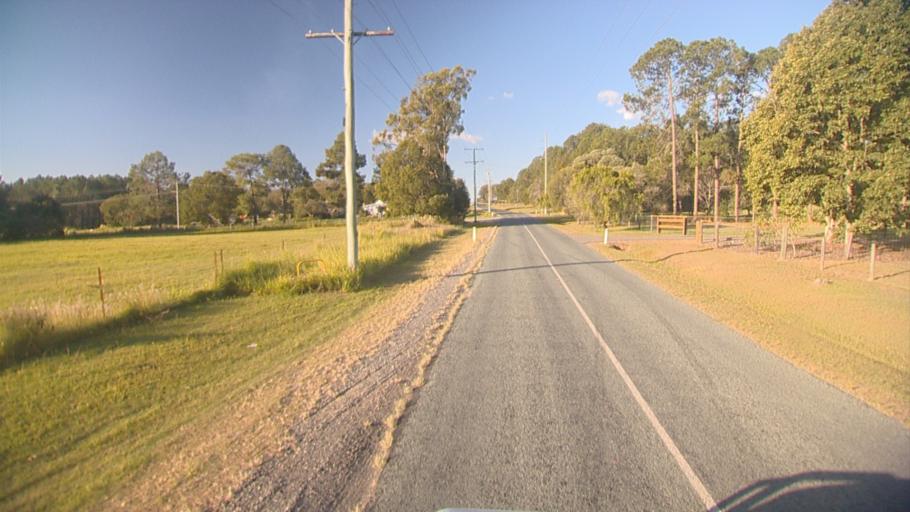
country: AU
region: Queensland
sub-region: Logan
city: Logan Reserve
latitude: -27.7263
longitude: 153.1004
